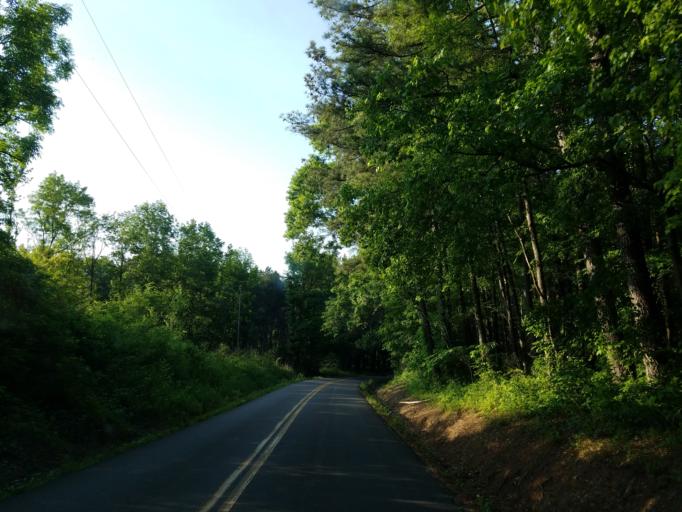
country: US
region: Georgia
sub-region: Gordon County
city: Calhoun
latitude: 34.5134
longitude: -85.1202
